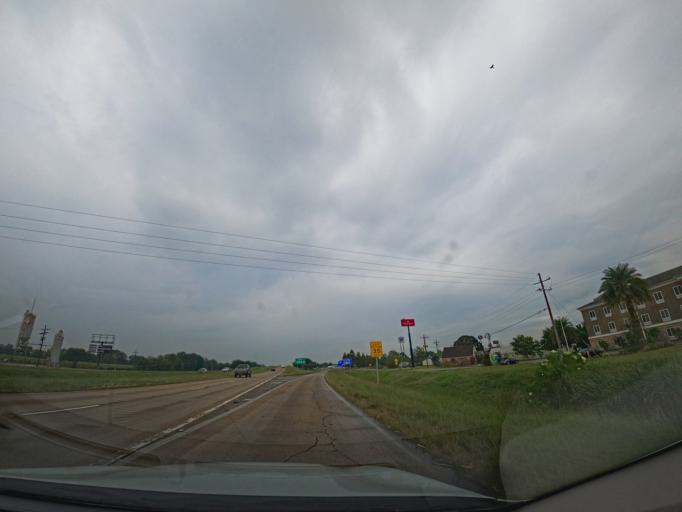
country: US
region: Louisiana
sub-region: Iberia Parish
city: New Iberia
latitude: 29.9828
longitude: -91.8559
